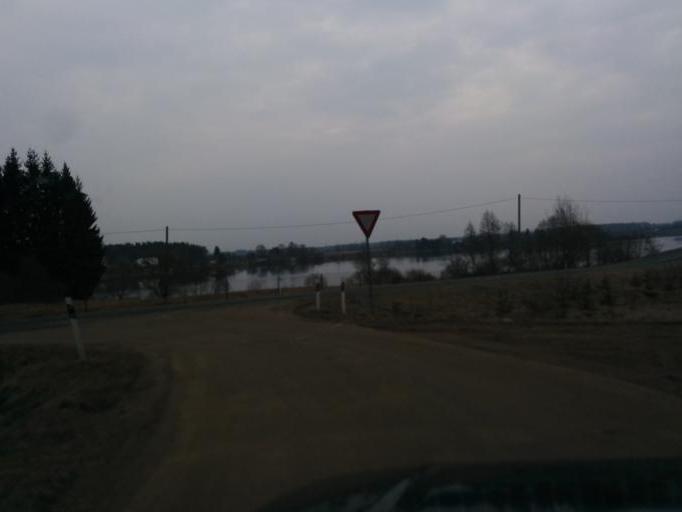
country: LV
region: Ogre
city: Ogre
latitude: 56.7843
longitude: 24.6116
